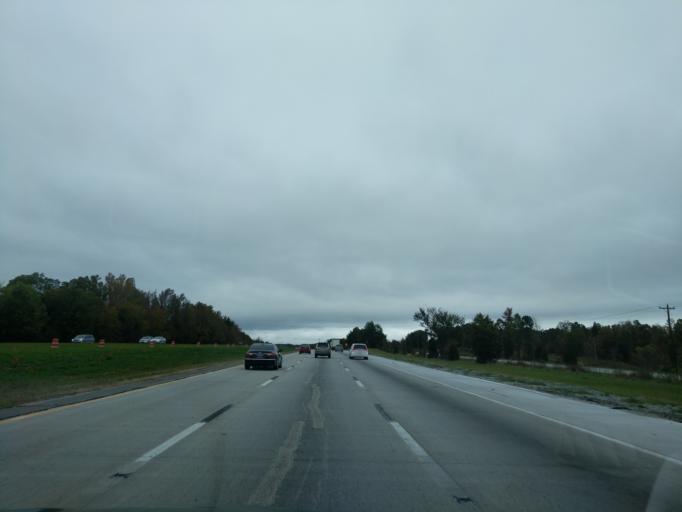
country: US
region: North Carolina
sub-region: Guilford County
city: Jamestown
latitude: 35.9571
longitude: -79.8962
